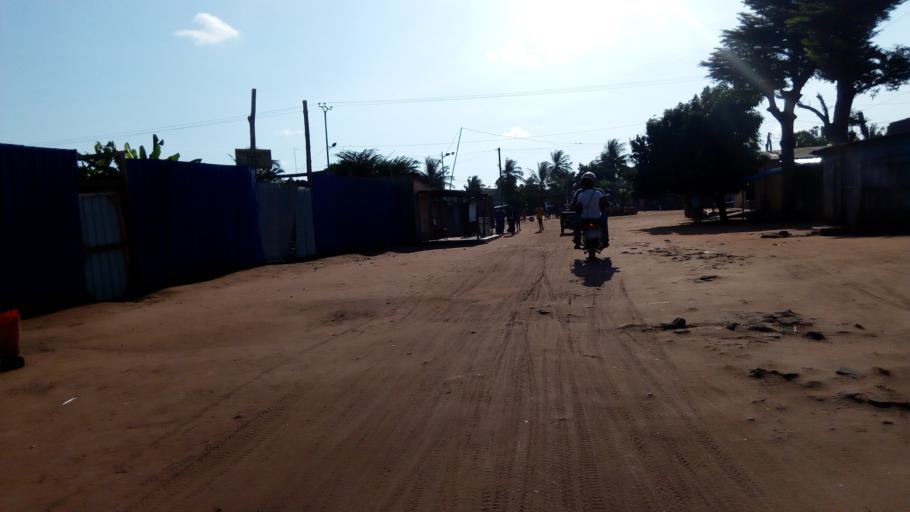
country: TG
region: Maritime
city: Lome
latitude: 6.2306
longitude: 1.1899
